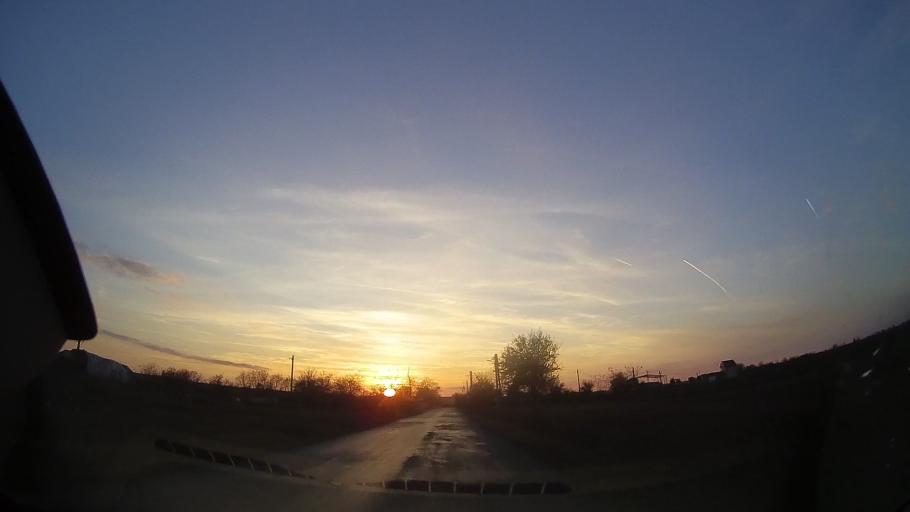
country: RO
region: Constanta
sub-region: Comuna Mereni
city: Mereni
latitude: 44.0163
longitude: 28.3333
